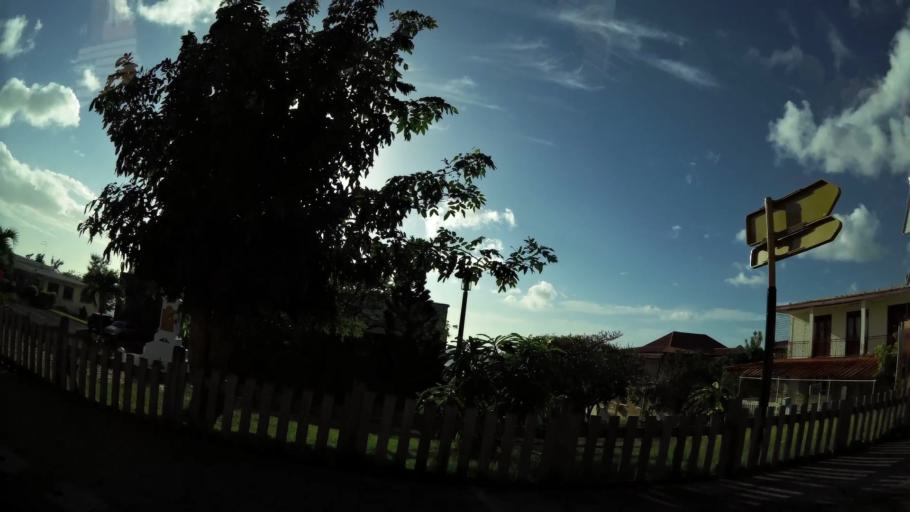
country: GP
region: Guadeloupe
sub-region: Guadeloupe
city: Pointe-Noire
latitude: 16.2333
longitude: -61.7901
